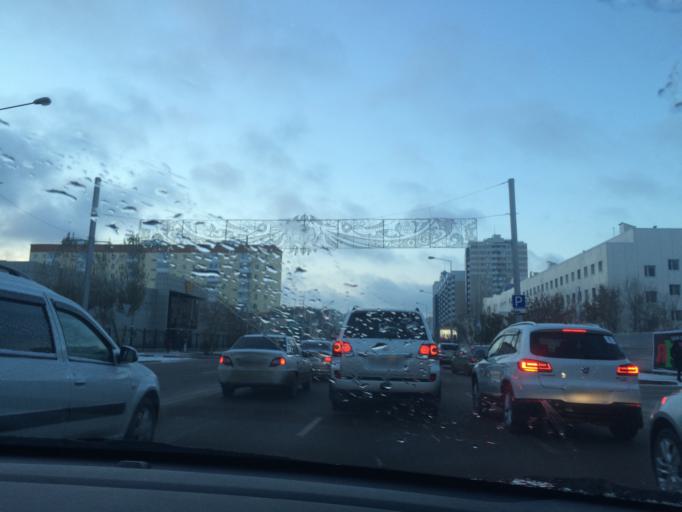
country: KZ
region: Astana Qalasy
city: Astana
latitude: 51.1712
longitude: 71.4074
